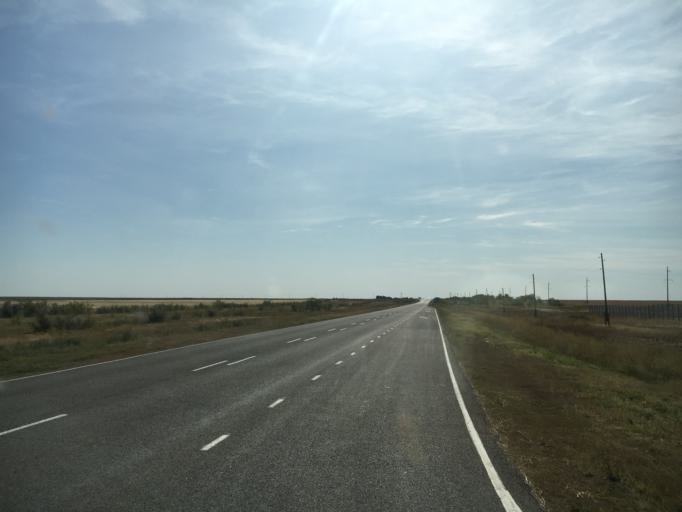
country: KZ
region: Batys Qazaqstan
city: Peremetnoe
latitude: 51.1328
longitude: 50.9002
